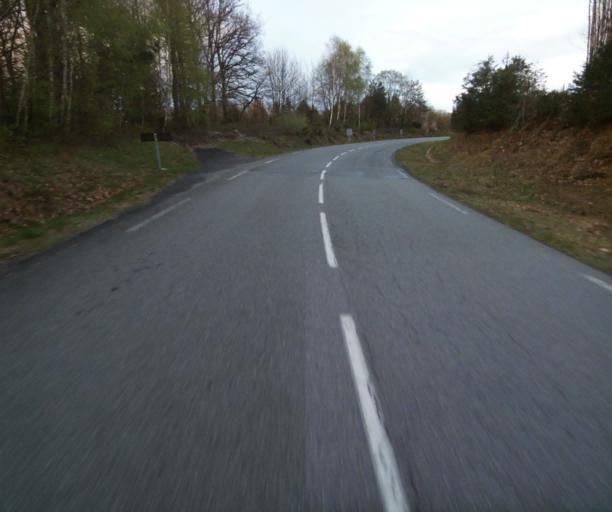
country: FR
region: Limousin
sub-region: Departement de la Correze
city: Laguenne
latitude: 45.2873
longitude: 1.8506
